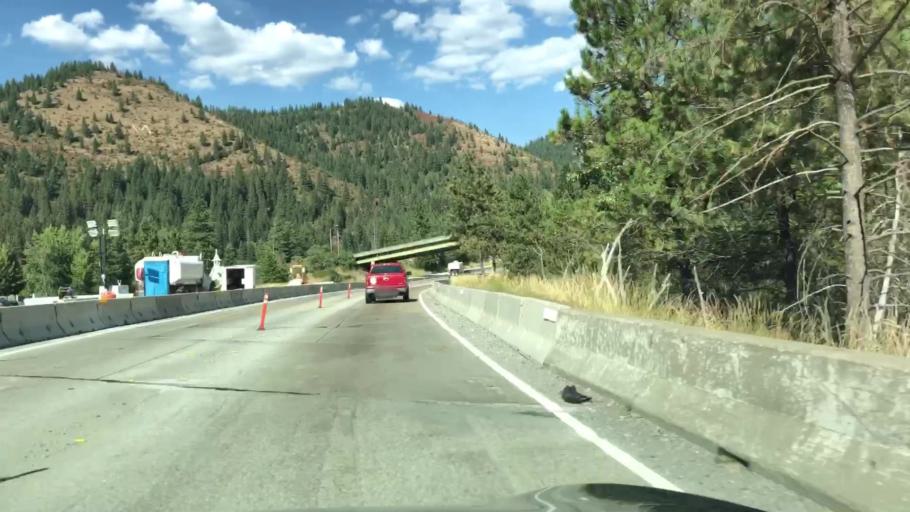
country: US
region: Idaho
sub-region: Shoshone County
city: Wallace
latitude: 47.4667
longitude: -115.8009
